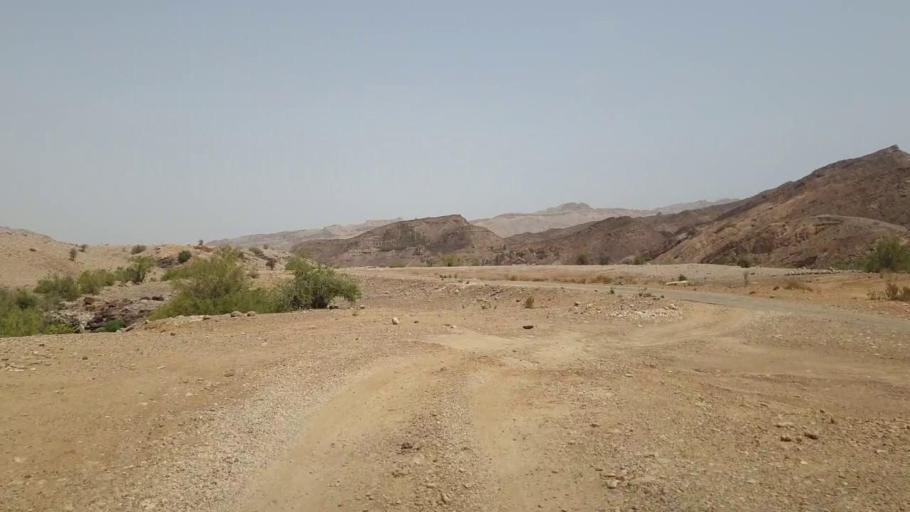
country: PK
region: Sindh
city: Sann
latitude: 25.8858
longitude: 67.9203
